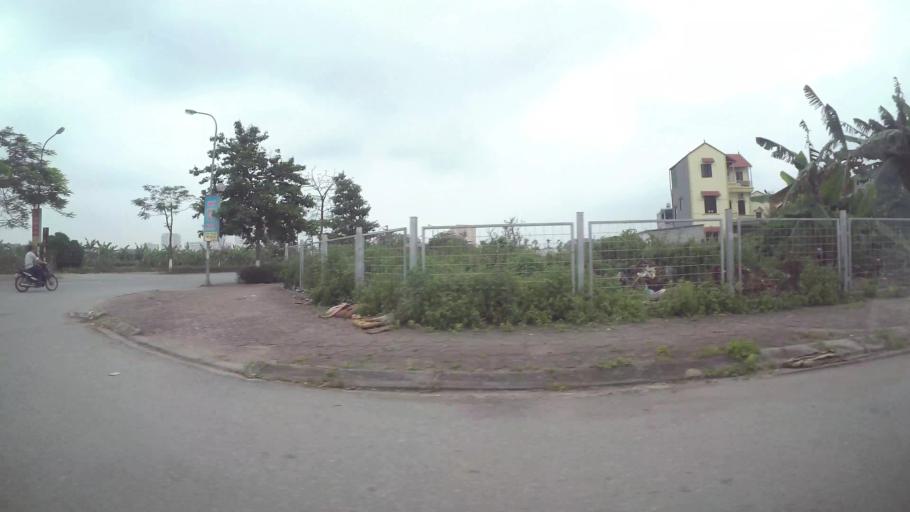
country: VN
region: Ha Noi
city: Trau Quy
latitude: 21.0529
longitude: 105.9206
